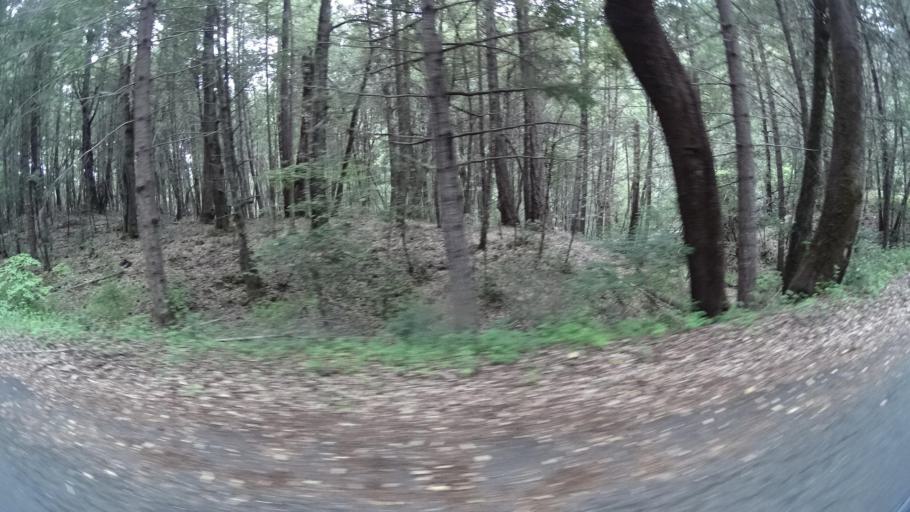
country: US
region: California
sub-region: Humboldt County
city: Willow Creek
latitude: 41.3457
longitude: -123.5109
